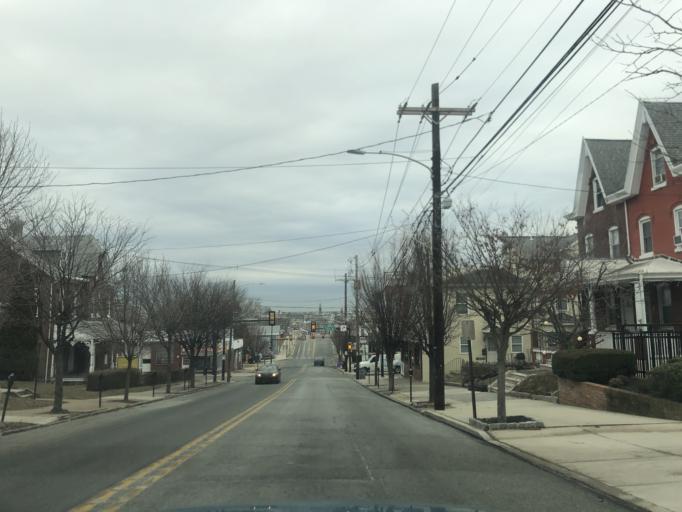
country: US
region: Pennsylvania
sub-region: Montgomery County
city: Bridgeport
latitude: 40.1045
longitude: -75.3475
